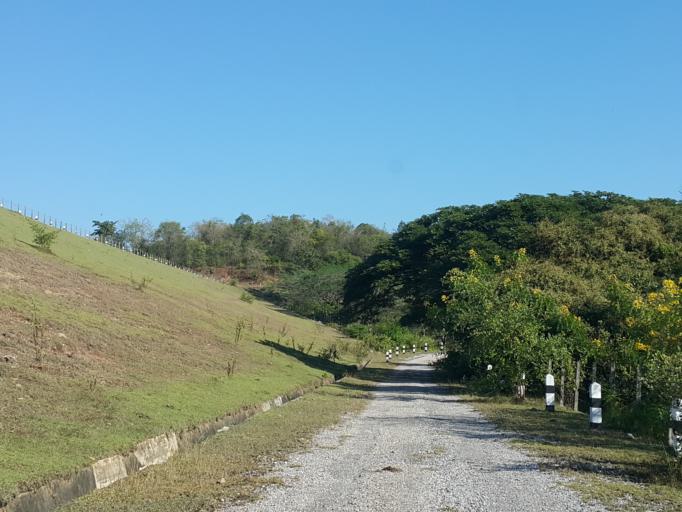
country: TH
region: Lampang
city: Mae Mo
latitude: 18.3094
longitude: 99.6547
